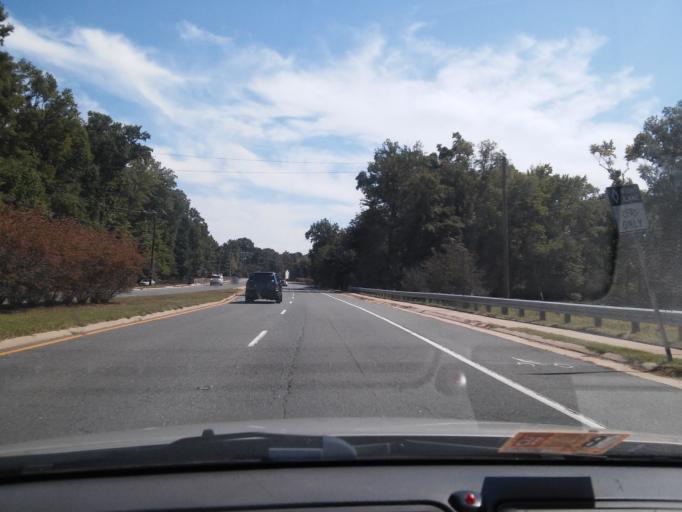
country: US
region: Virginia
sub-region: Chesterfield County
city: Bon Air
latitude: 37.5168
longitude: -77.5967
